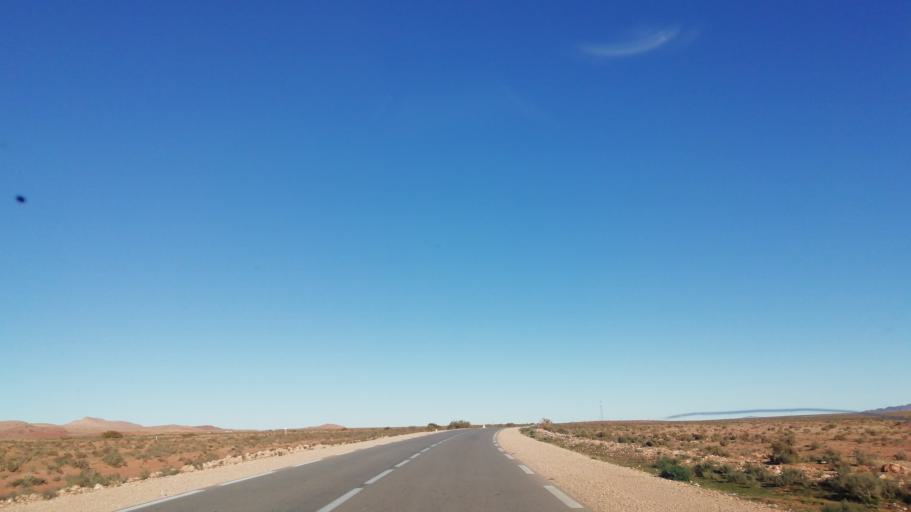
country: DZ
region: El Bayadh
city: El Abiodh Sidi Cheikh
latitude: 33.1111
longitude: 0.2250
